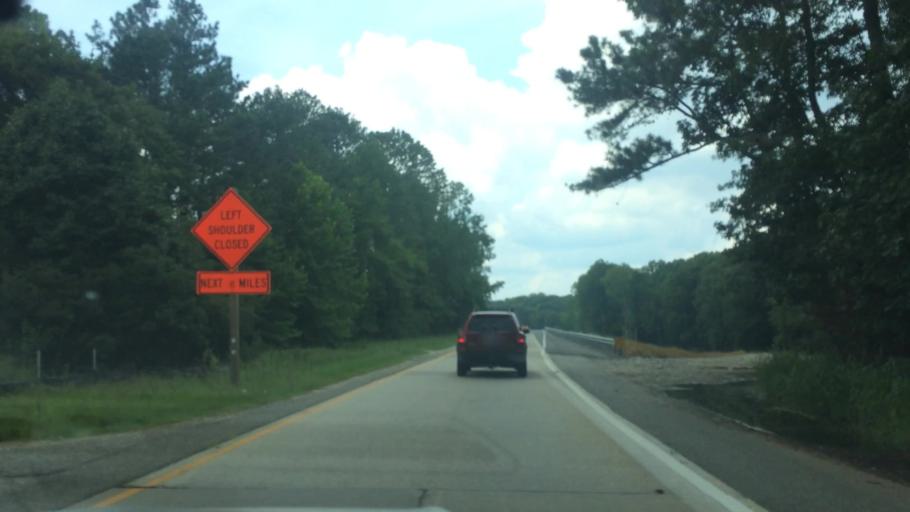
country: US
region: Virginia
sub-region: York County
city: Yorktown
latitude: 37.2132
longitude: -76.5868
